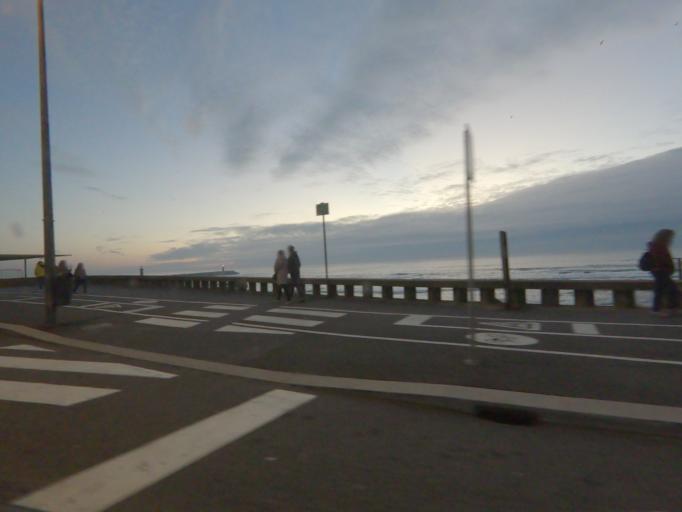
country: PT
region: Porto
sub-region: Matosinhos
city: Matosinhos
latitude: 41.1499
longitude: -8.6763
